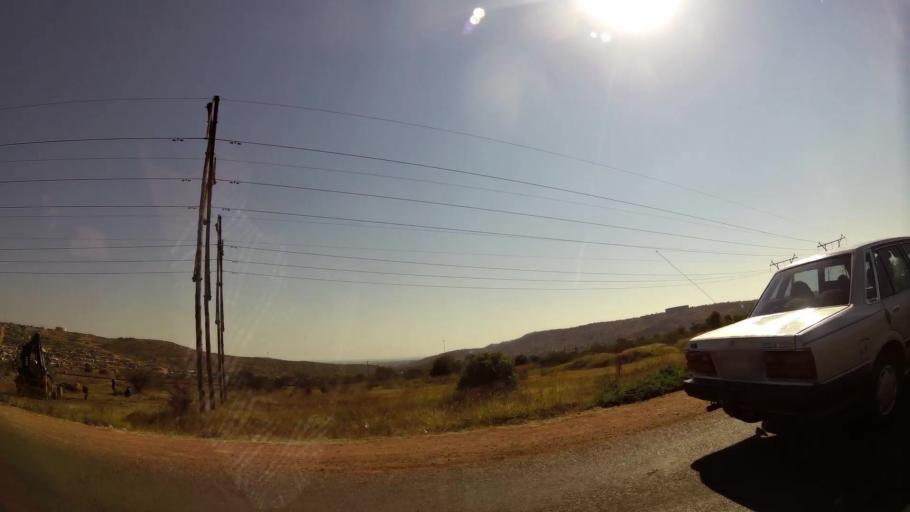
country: ZA
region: Gauteng
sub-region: City of Tshwane Metropolitan Municipality
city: Mabopane
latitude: -25.5410
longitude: 28.0793
